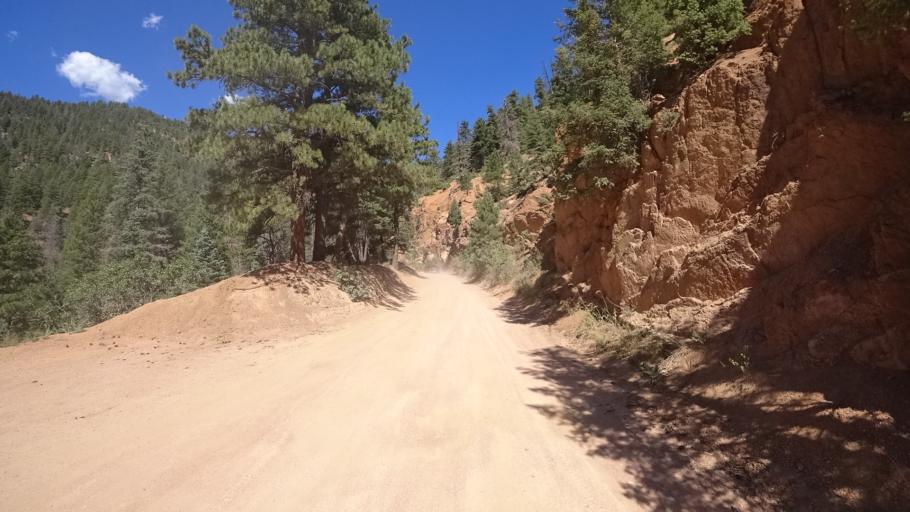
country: US
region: Colorado
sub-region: El Paso County
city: Manitou Springs
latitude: 38.7940
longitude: -104.8960
